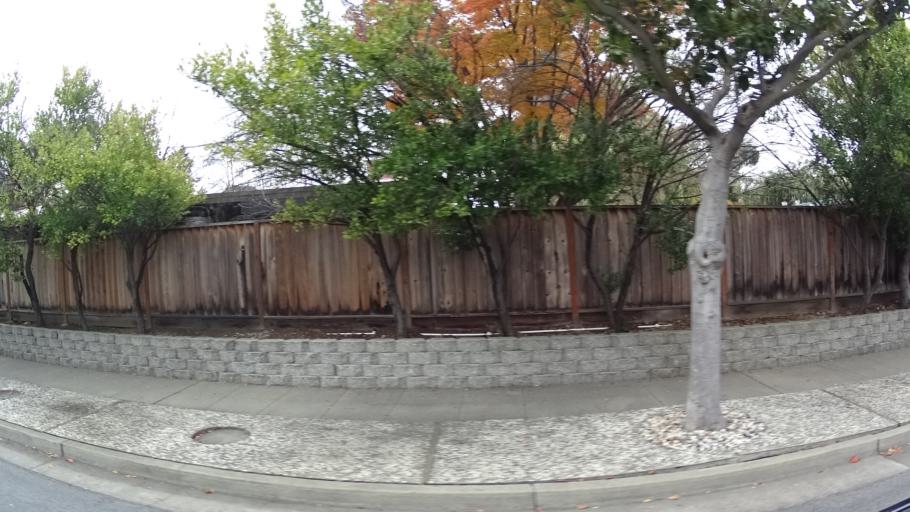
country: US
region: California
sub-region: Santa Clara County
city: Sunnyvale
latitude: 37.3548
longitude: -122.0386
